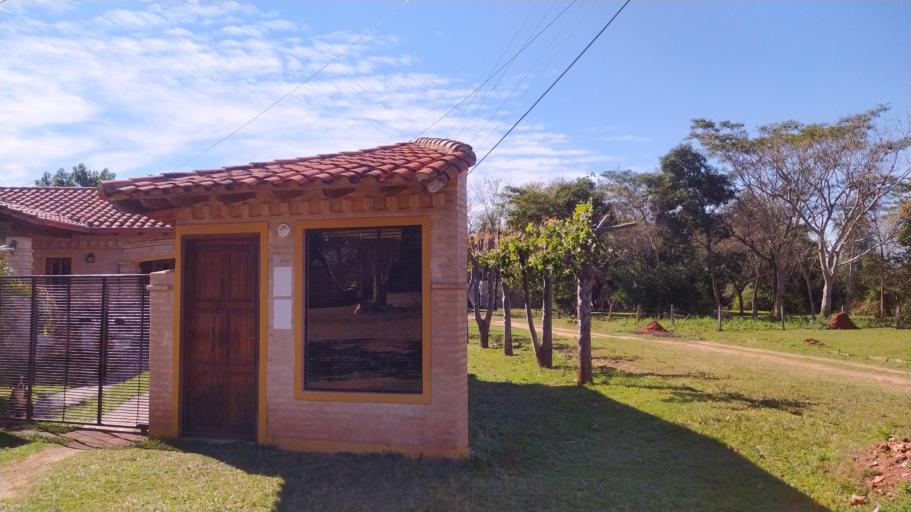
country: PY
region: Misiones
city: San Juan Bautista
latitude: -26.6771
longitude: -57.1397
